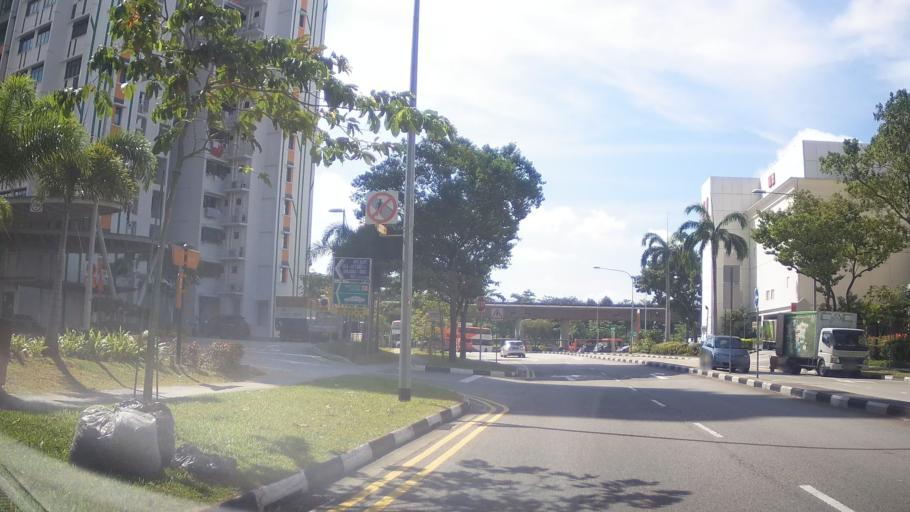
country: MY
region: Johor
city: Johor Bahru
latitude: 1.3407
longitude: 103.7071
